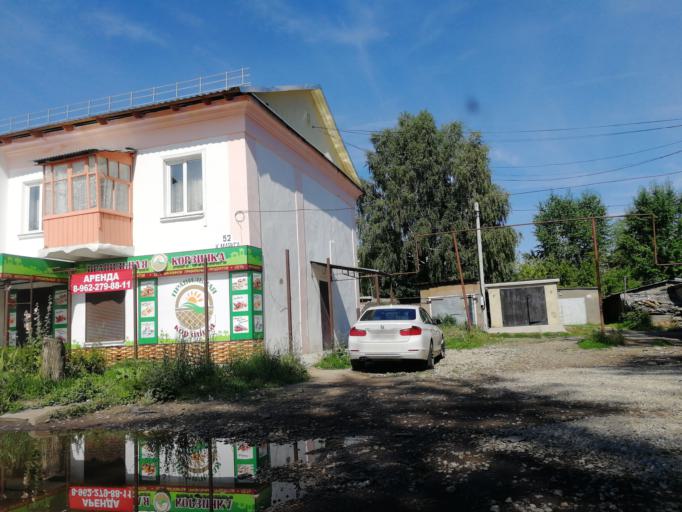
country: RU
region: Tula
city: Bogoroditsk
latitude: 53.7683
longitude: 38.1222
